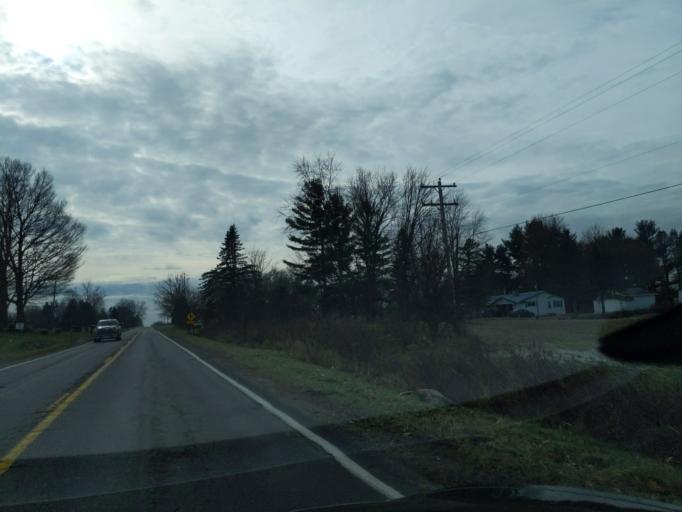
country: US
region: Michigan
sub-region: Ingham County
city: Holt
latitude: 42.6206
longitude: -84.5231
